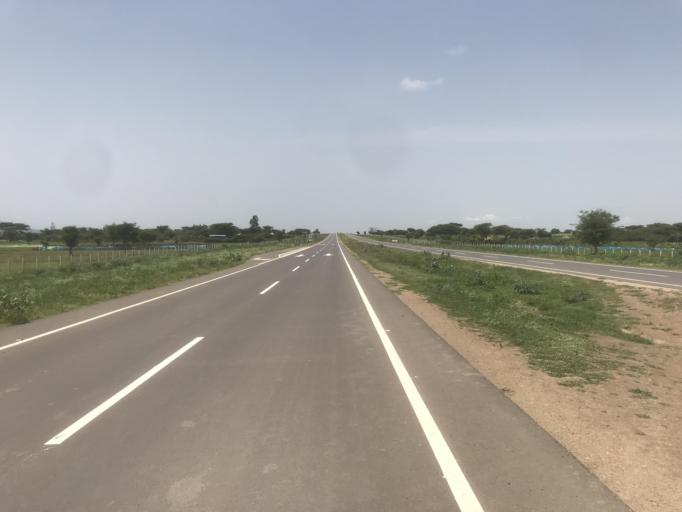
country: ET
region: Oromiya
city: Mojo
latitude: 8.3713
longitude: 38.9972
